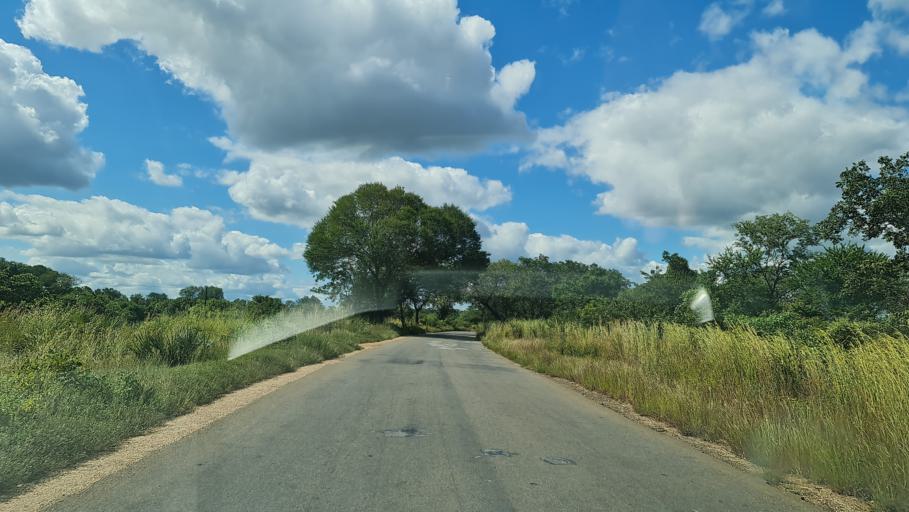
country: MZ
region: Zambezia
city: Quelimane
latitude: -17.5105
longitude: 36.2292
